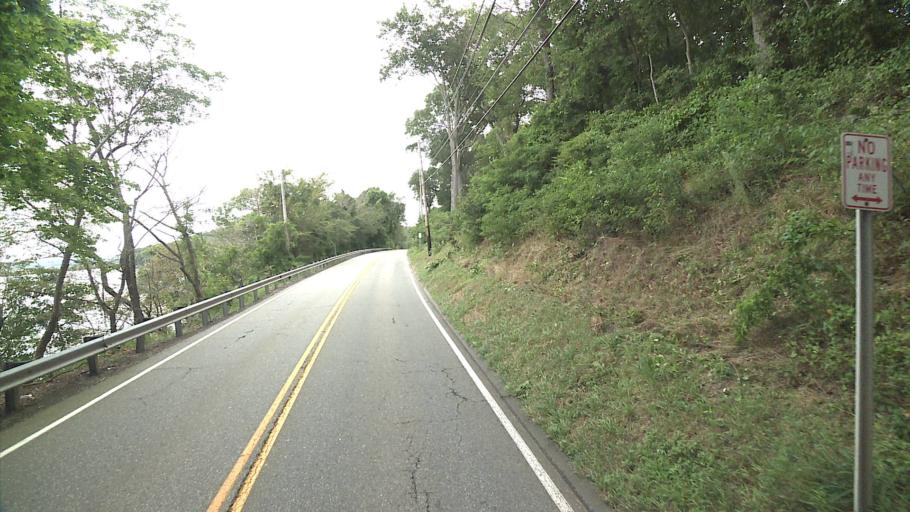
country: US
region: Connecticut
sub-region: Middlesex County
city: Old Saybrook Center
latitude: 41.3261
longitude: -72.3412
